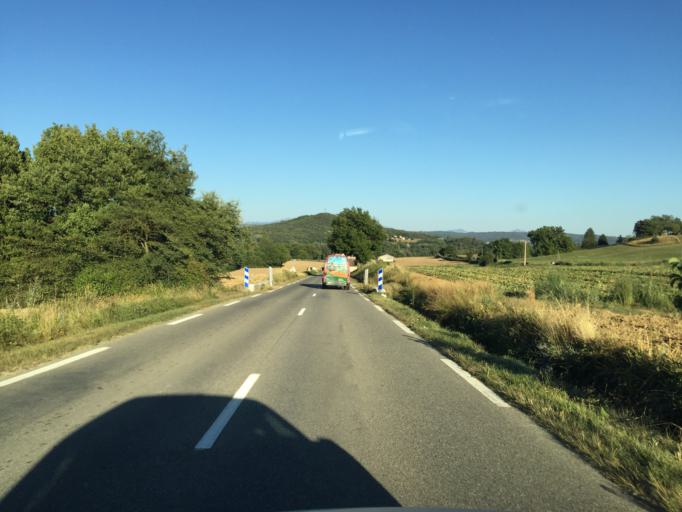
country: FR
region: Provence-Alpes-Cote d'Azur
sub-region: Departement des Alpes-de-Haute-Provence
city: Villeneuve
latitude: 43.9530
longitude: 5.8509
